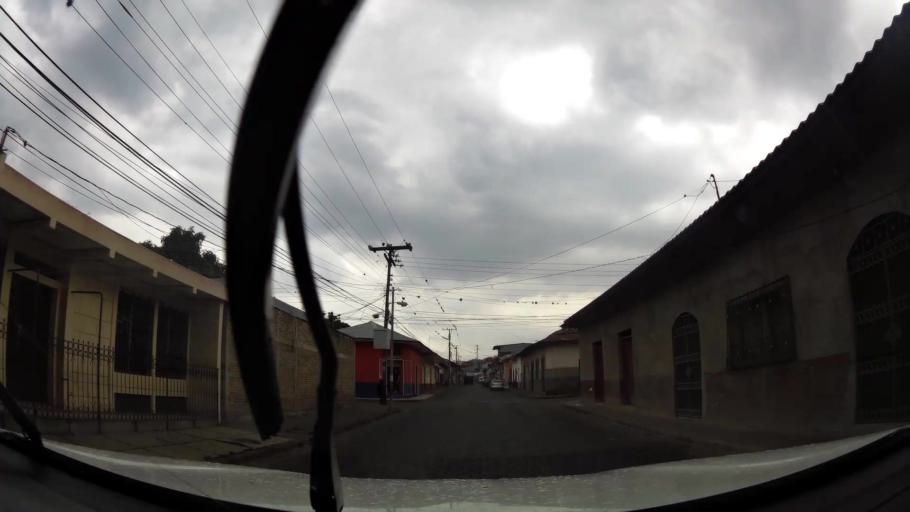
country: NI
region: Jinotega
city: Jinotega
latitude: 13.0971
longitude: -86.0026
